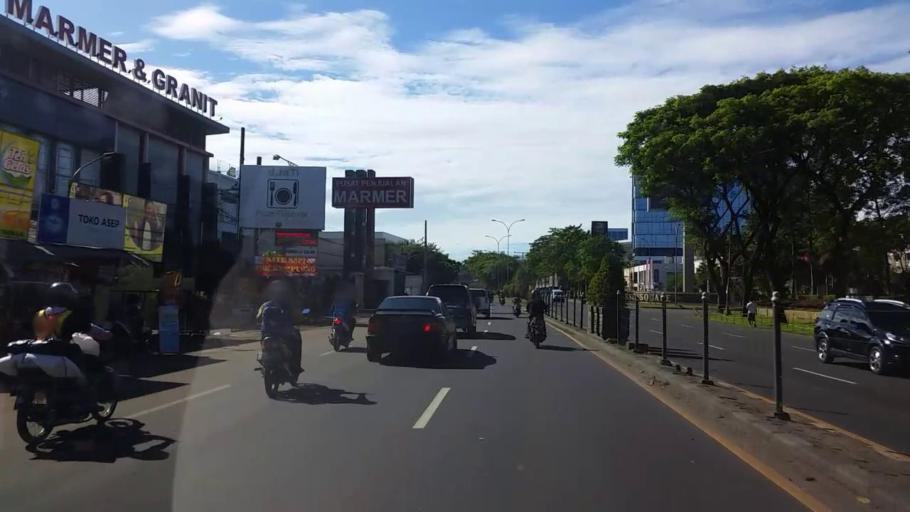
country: ID
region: West Java
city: Serpong
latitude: -6.2921
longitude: 106.6660
